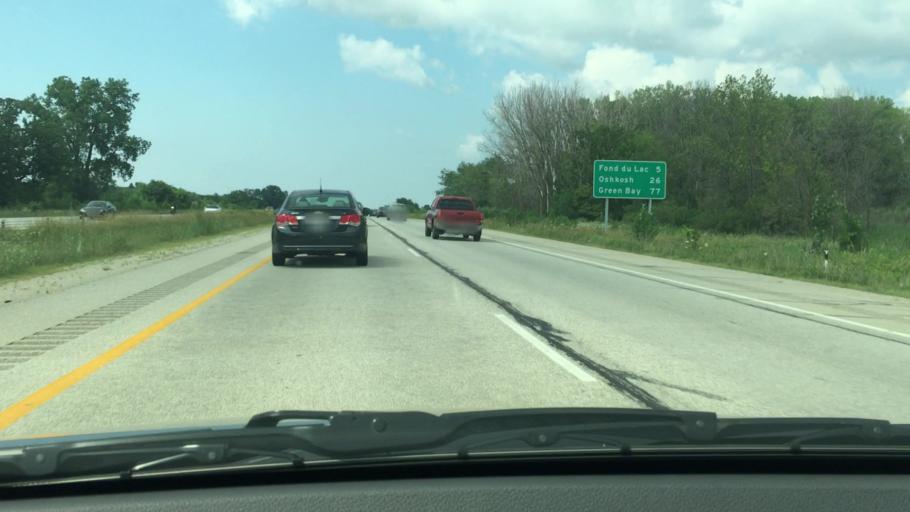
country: US
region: Wisconsin
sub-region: Fond du Lac County
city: Fond du Lac
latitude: 43.7033
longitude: -88.4421
